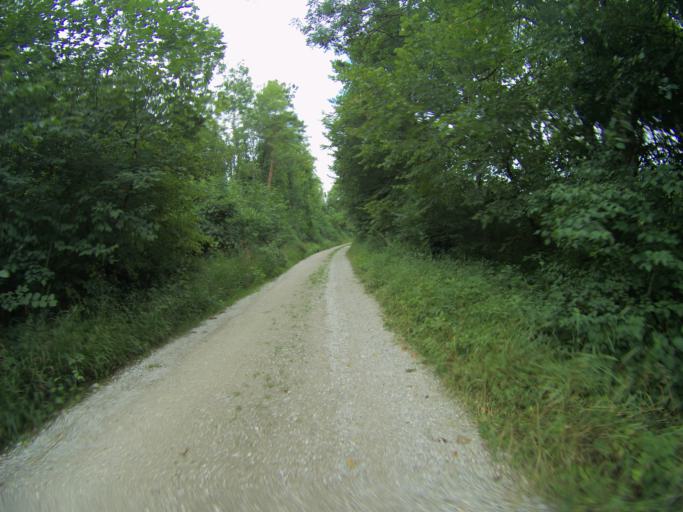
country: DE
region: Bavaria
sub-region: Upper Bavaria
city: Hallbergmoos
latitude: 48.3589
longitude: 11.7365
